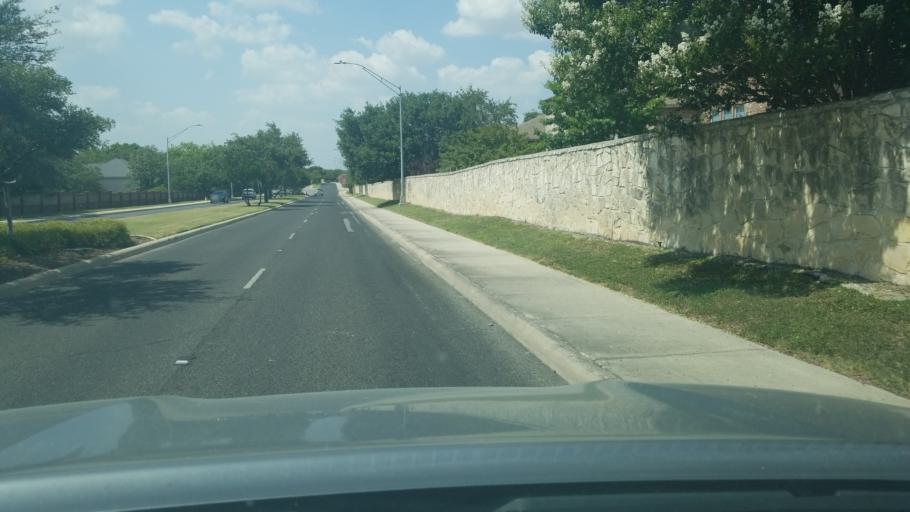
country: US
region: Texas
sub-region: Bexar County
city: Hollywood Park
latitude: 29.6492
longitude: -98.4948
